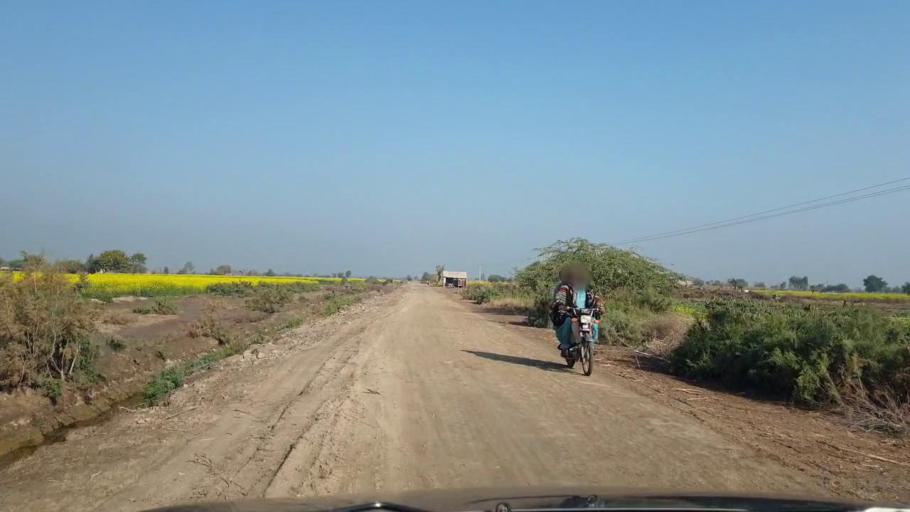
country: PK
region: Sindh
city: Sinjhoro
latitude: 26.0413
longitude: 68.7887
